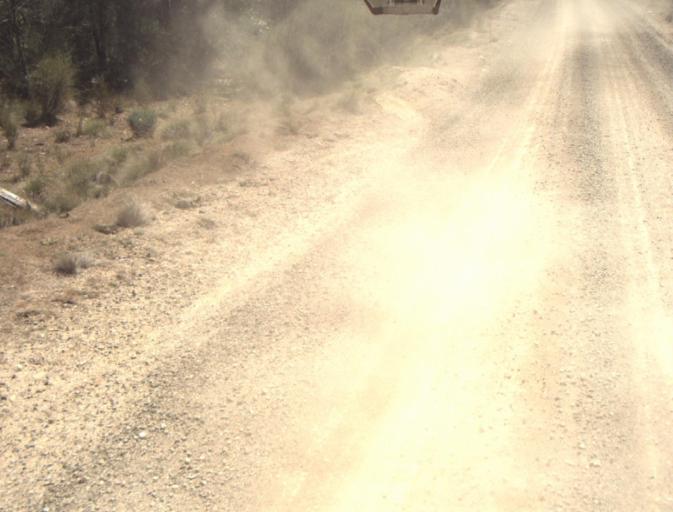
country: AU
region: Tasmania
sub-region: Dorset
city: Scottsdale
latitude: -41.3238
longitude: 147.4662
